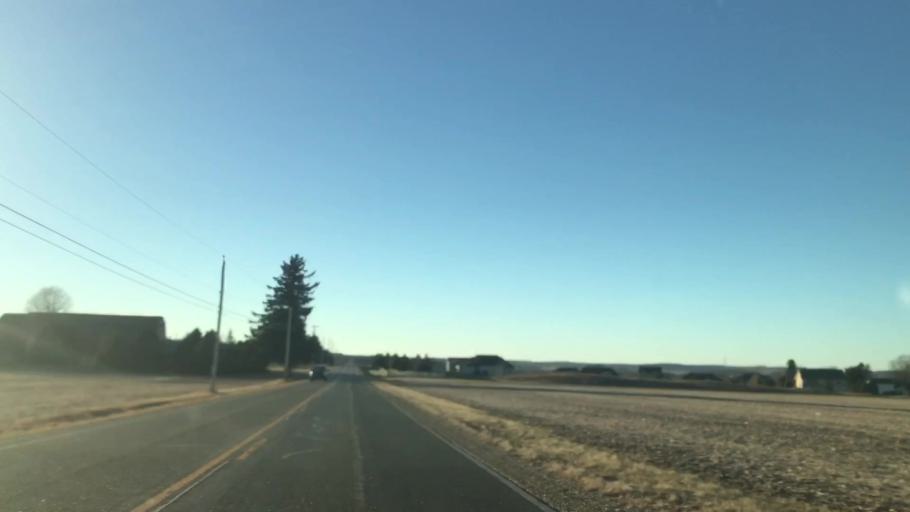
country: US
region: Wisconsin
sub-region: Washington County
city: Jackson
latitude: 43.2948
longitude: -88.1475
